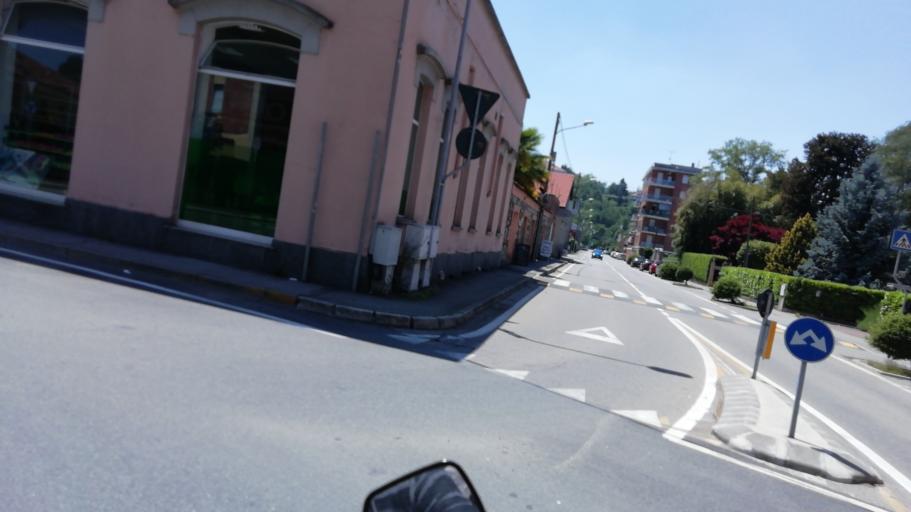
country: IT
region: Piedmont
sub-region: Provincia di Novara
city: Borgomanero
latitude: 45.6966
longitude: 8.4574
